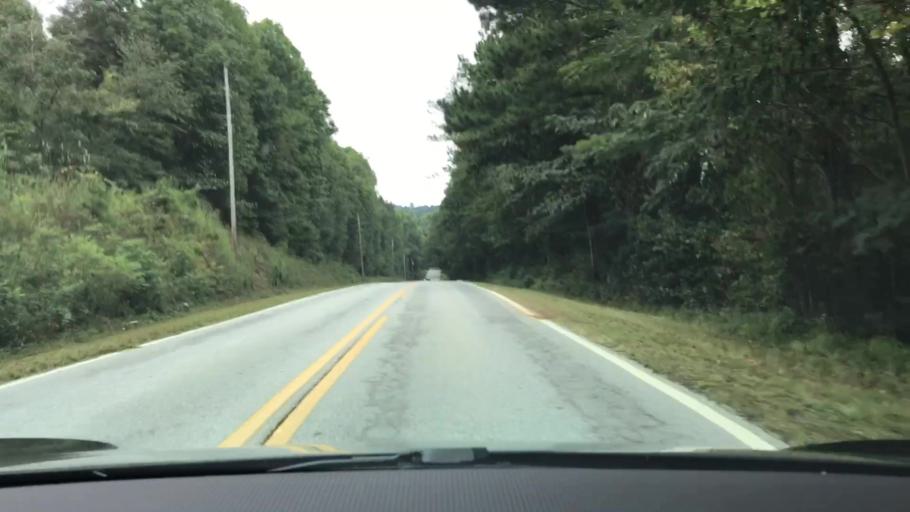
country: US
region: Georgia
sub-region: Barrow County
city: Auburn
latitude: 34.0531
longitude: -83.8212
